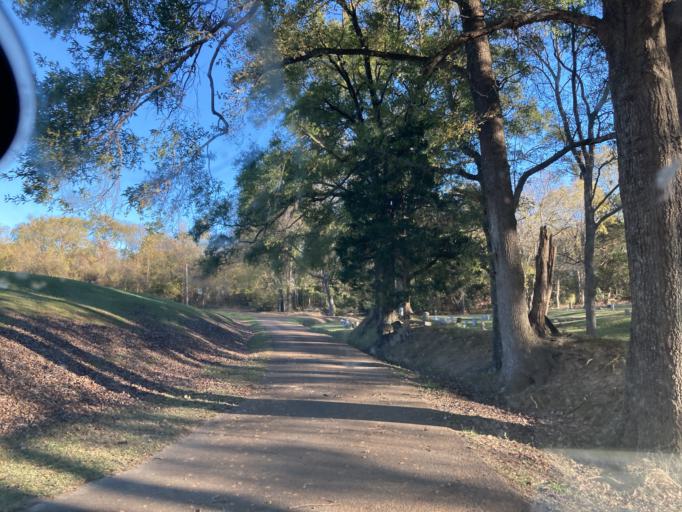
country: US
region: Mississippi
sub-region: Yazoo County
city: Yazoo City
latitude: 32.8502
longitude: -90.3985
